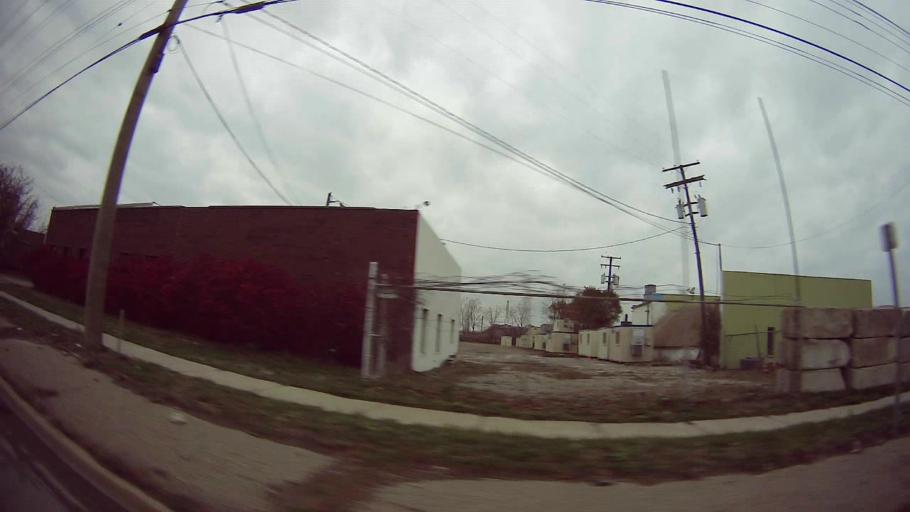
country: US
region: Michigan
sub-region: Macomb County
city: Warren
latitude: 42.4586
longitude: -82.9957
